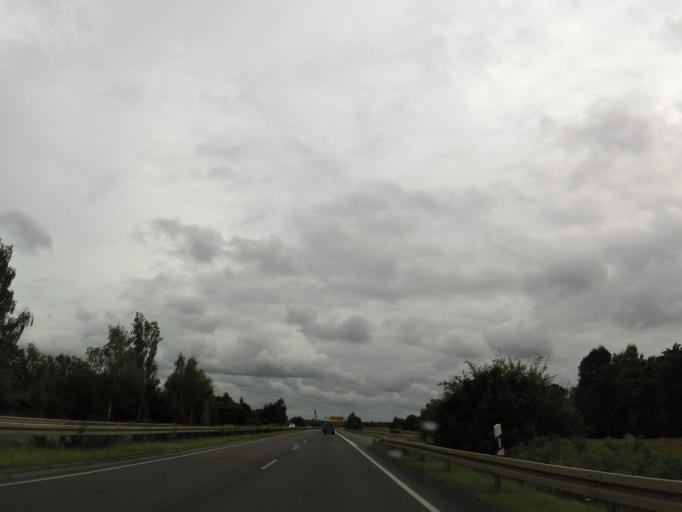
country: DE
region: Saxony
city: Markkleeberg
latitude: 51.2632
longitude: 12.3821
